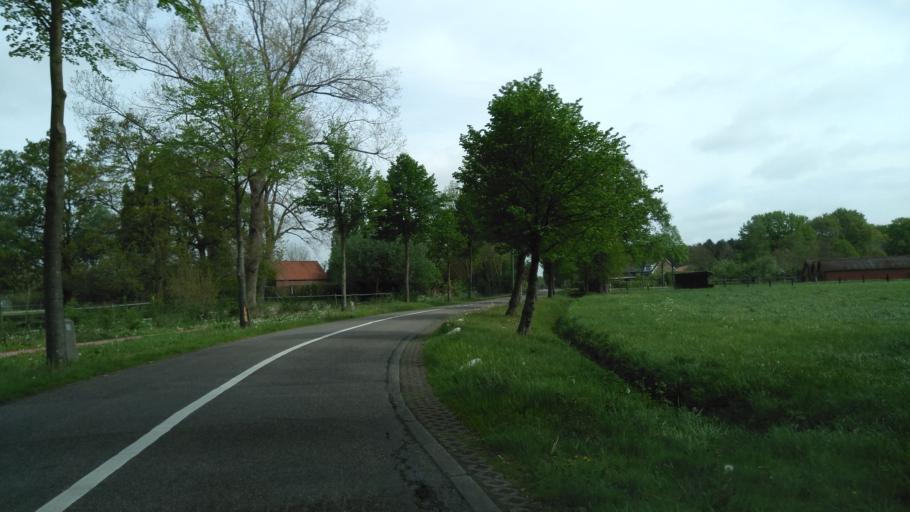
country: BE
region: Flanders
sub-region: Provincie Antwerpen
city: Baarle-Hertog
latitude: 51.4125
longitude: 4.9003
